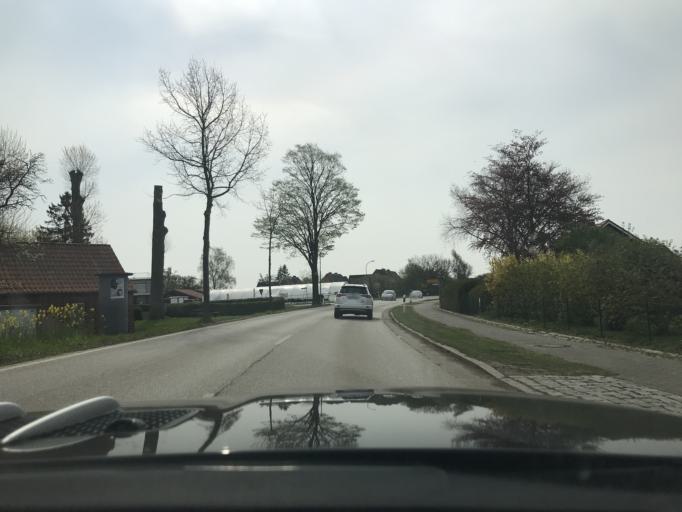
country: DE
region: Schleswig-Holstein
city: Heringsdorf
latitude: 54.2799
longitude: 11.0306
